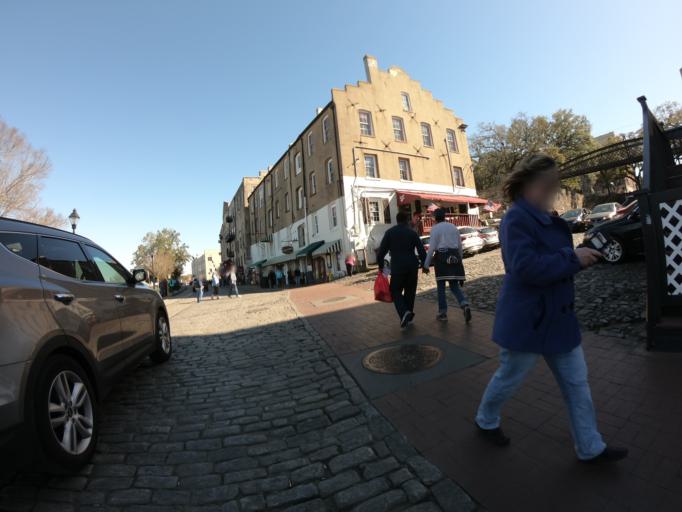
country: US
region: Georgia
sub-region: Chatham County
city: Savannah
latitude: 32.0810
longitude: -81.0888
